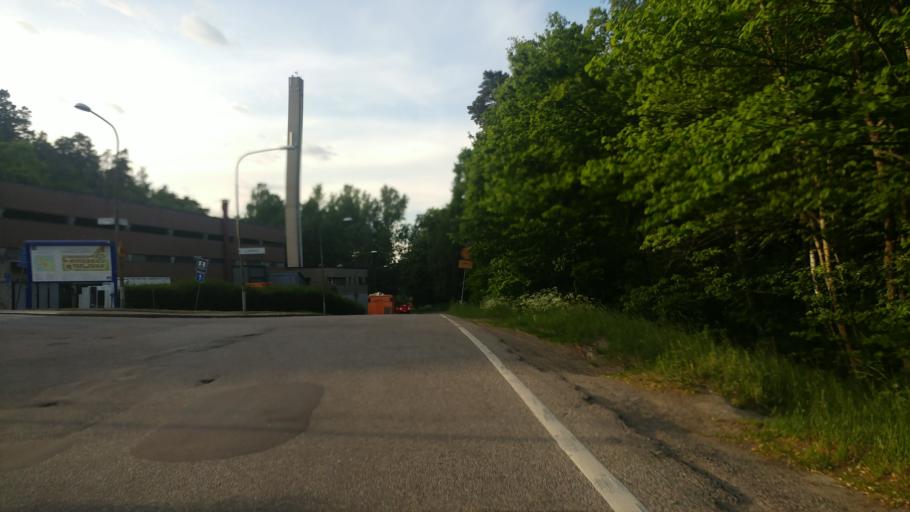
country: SE
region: Stockholm
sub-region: Danderyds Kommun
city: Djursholm
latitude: 59.3703
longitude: 18.0679
